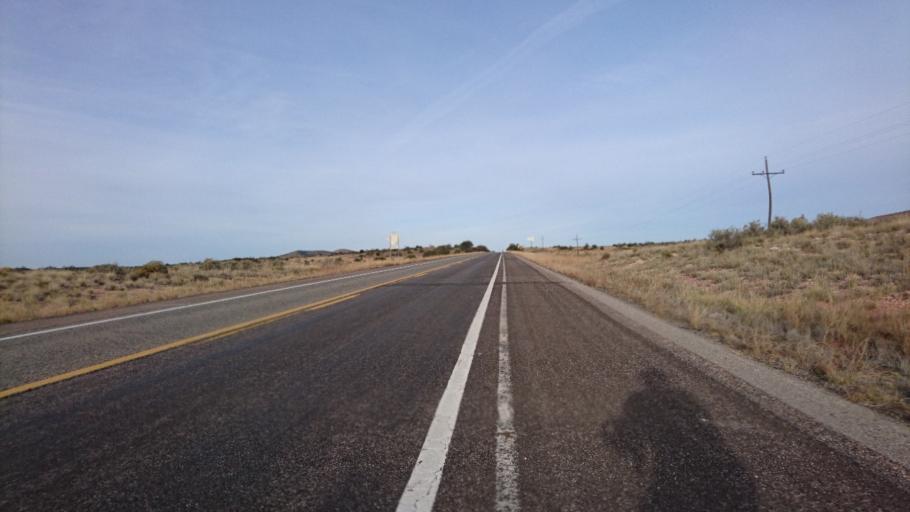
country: US
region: Arizona
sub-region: Mohave County
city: Peach Springs
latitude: 35.5334
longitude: -113.2431
